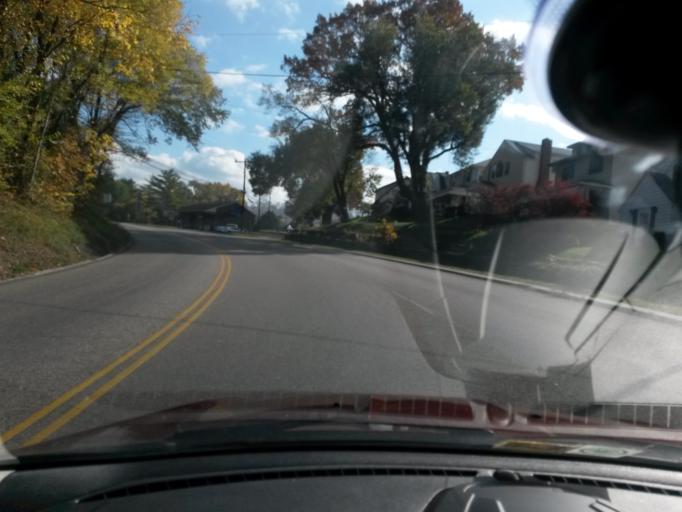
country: US
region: Virginia
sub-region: City of Covington
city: Fairlawn
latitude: 37.7784
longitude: -79.9866
